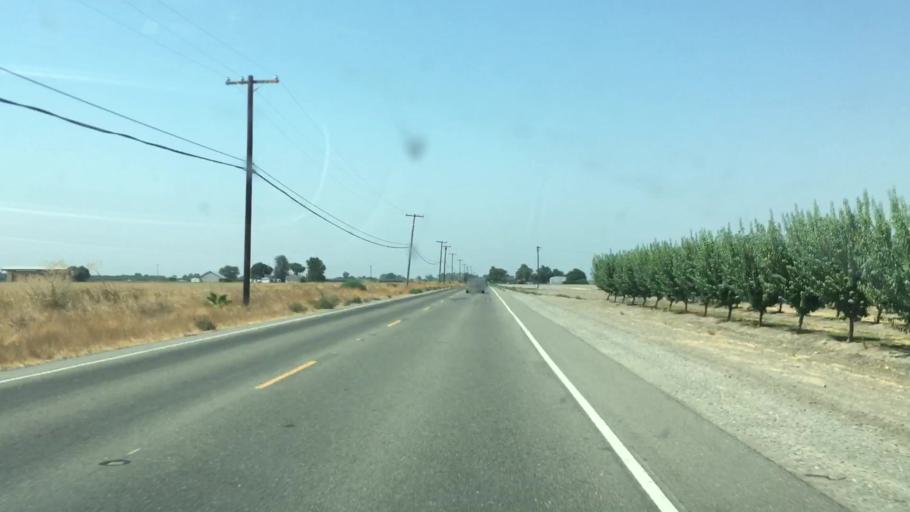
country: US
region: California
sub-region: San Joaquin County
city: Taft Mosswood
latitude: 37.8774
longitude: -121.3515
